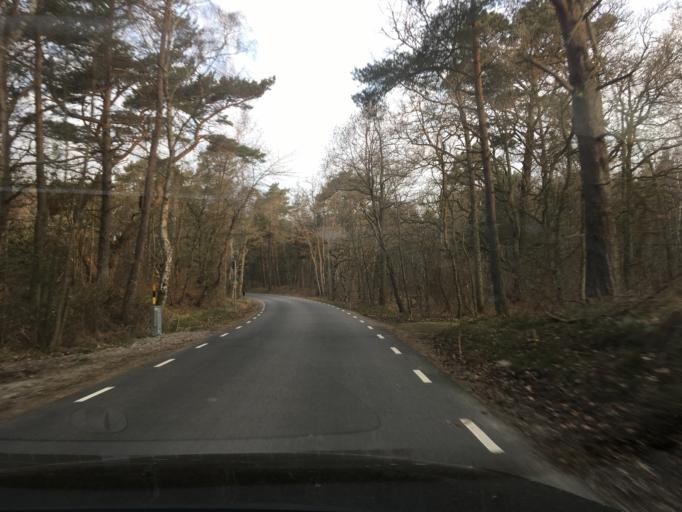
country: SE
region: Skane
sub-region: Simrishamns Kommun
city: Simrishamn
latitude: 55.3892
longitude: 14.1900
